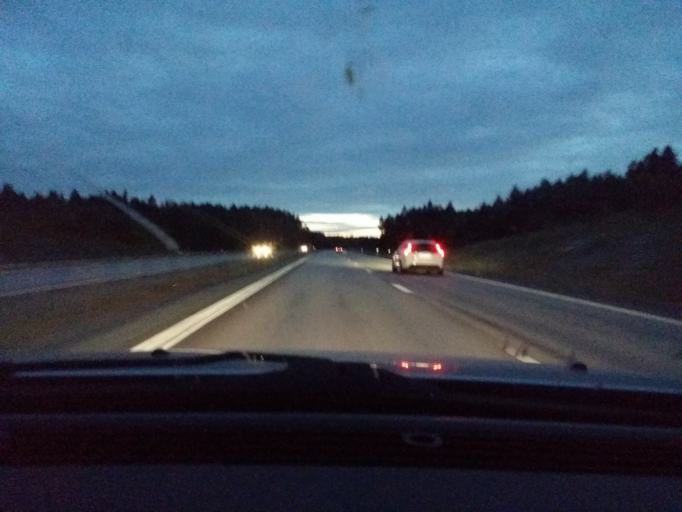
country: SE
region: Uppsala
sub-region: Enkopings Kommun
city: Hummelsta
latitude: 59.6276
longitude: 16.8348
